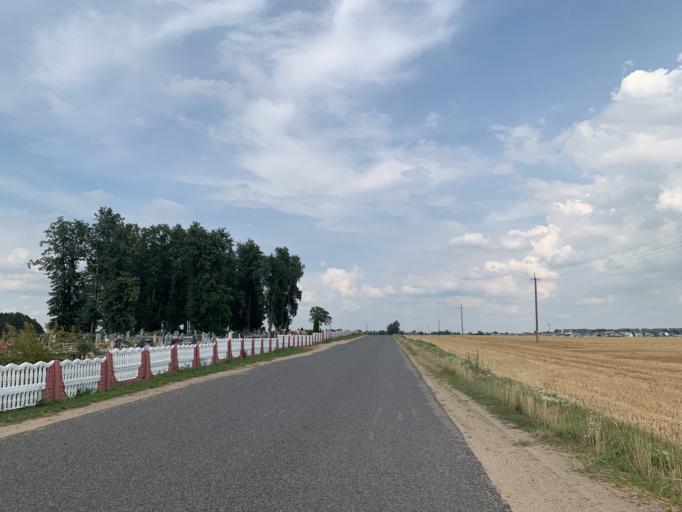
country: BY
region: Minsk
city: Nyasvizh
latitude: 53.1990
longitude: 26.6707
